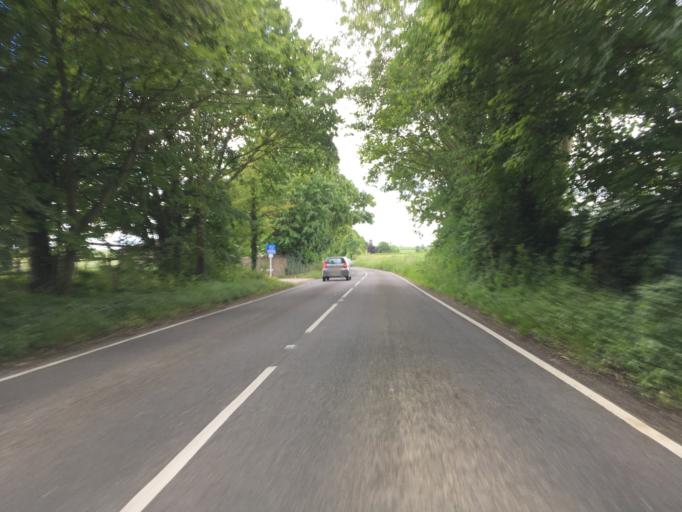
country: GB
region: England
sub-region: Oxfordshire
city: Shipton under Wychwood
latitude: 51.8524
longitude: -1.6014
